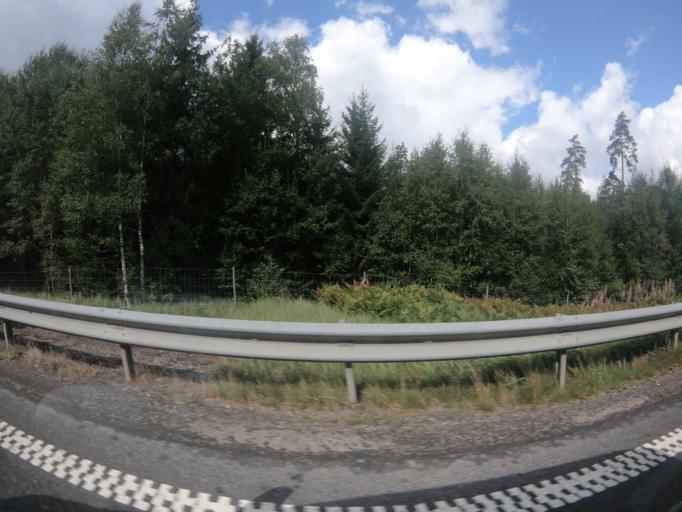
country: SE
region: Kronoberg
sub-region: Vaxjo Kommun
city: Rottne
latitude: 56.9682
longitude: 14.9682
